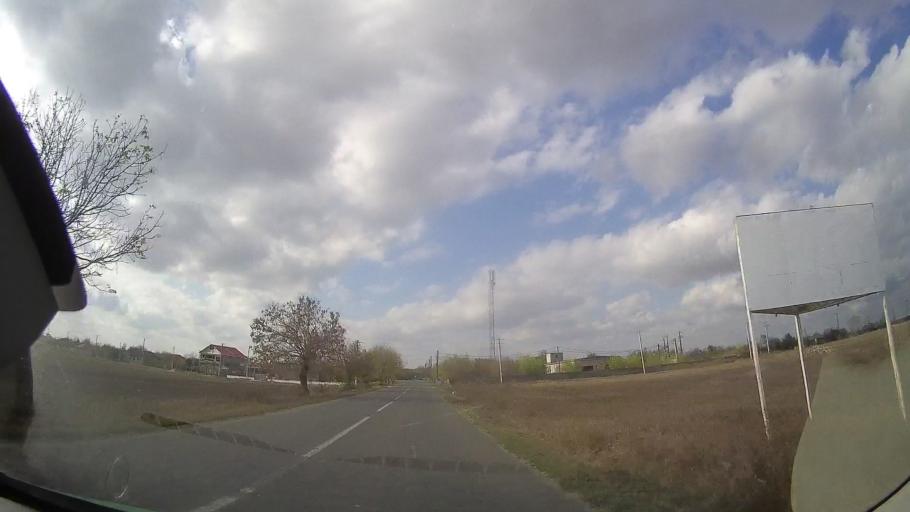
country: RO
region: Constanta
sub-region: Comuna Pecineaga
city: Pecineaga
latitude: 43.8972
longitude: 28.5146
